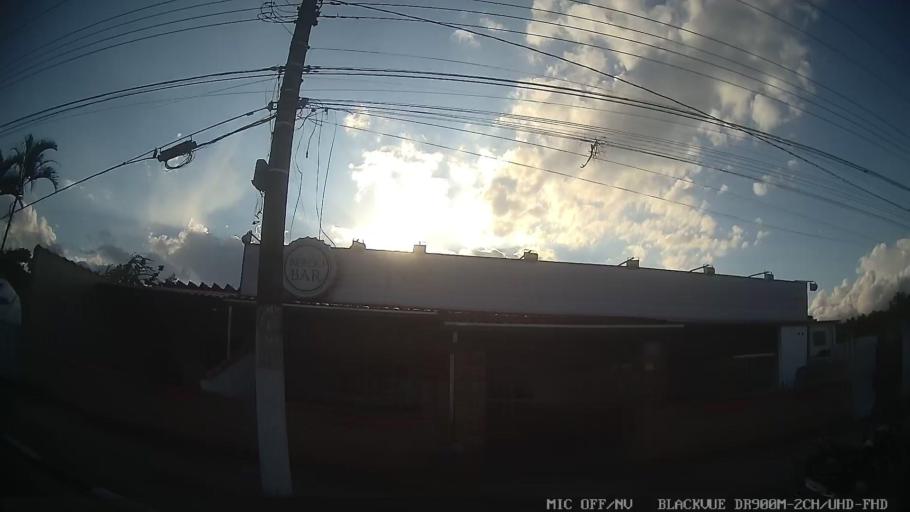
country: BR
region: Sao Paulo
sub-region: Caraguatatuba
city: Caraguatatuba
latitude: -23.6801
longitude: -45.4322
